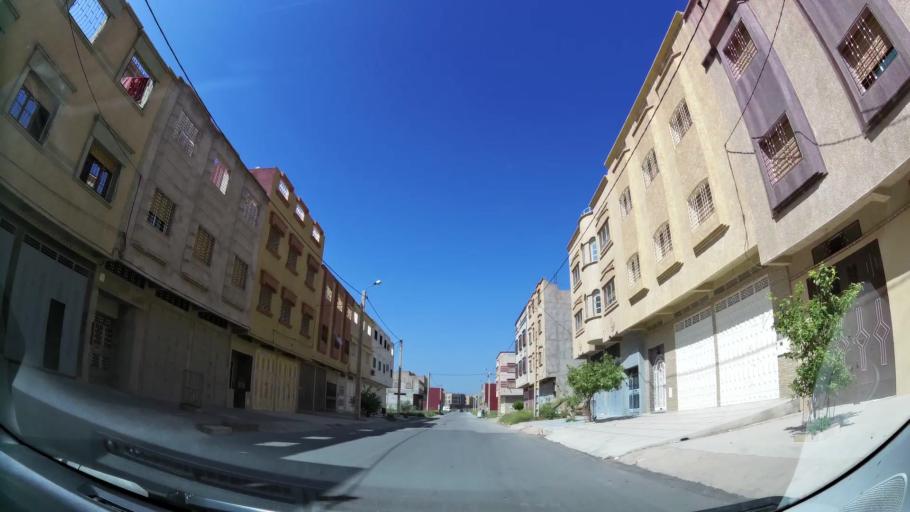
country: MA
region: Oriental
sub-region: Oujda-Angad
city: Oujda
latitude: 34.6748
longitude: -1.9352
